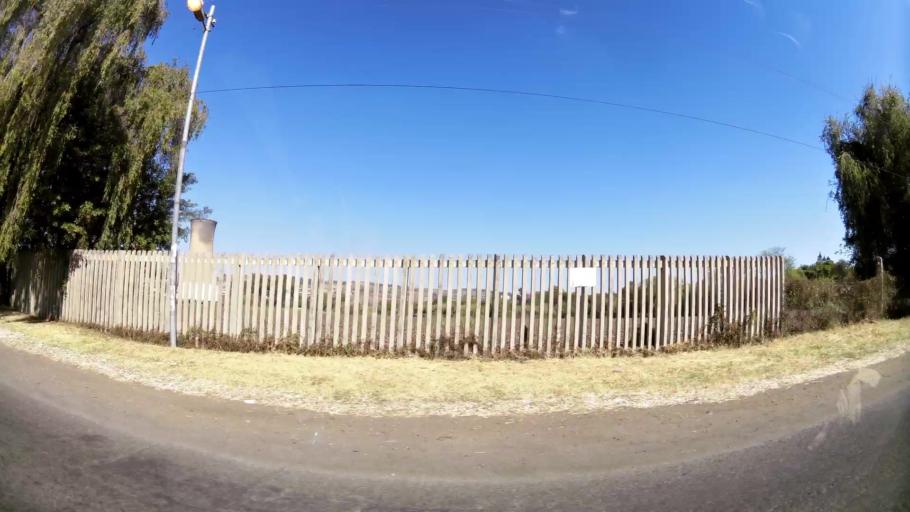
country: ZA
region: Gauteng
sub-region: City of Tshwane Metropolitan Municipality
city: Pretoria
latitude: -25.7551
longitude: 28.1445
